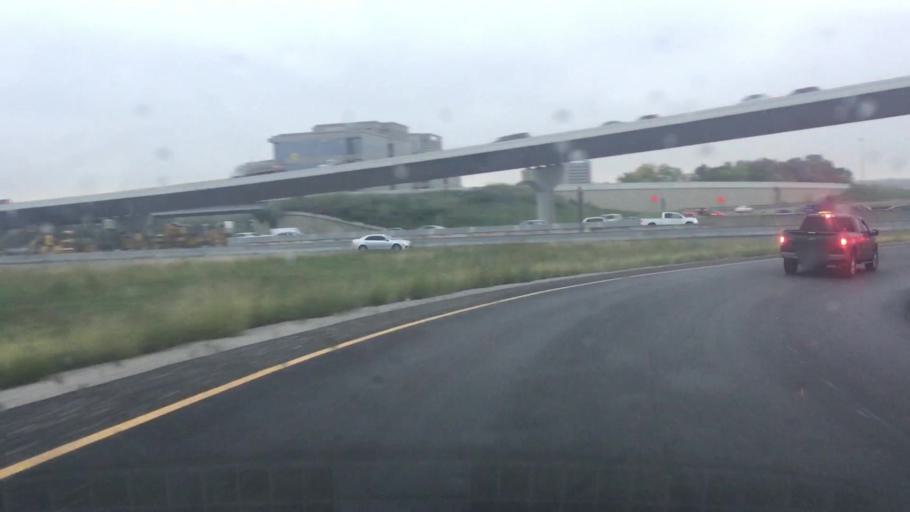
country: US
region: Kansas
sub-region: Johnson County
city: Lenexa
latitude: 38.9360
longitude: -94.7034
